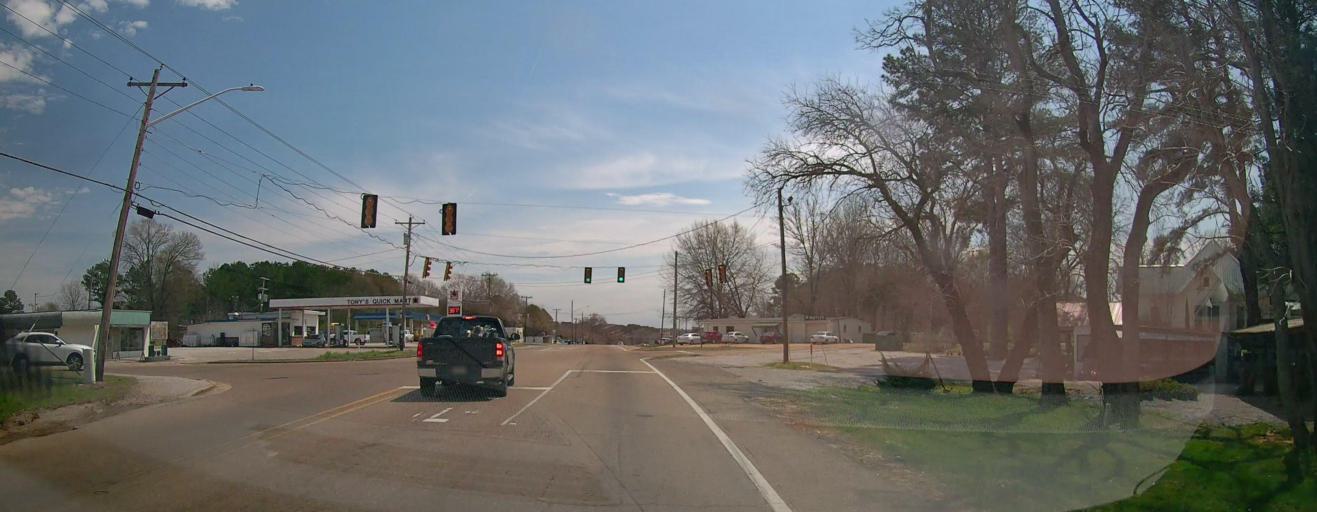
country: US
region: Mississippi
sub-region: Union County
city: New Albany
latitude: 34.5095
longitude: -89.0347
